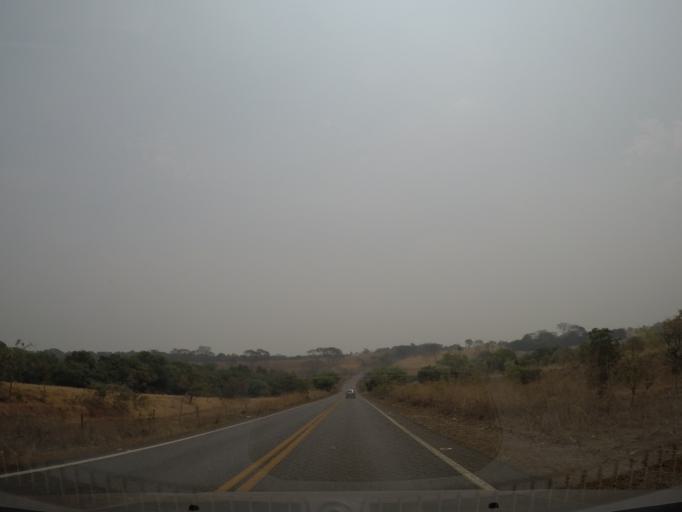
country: BR
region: Goias
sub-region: Pirenopolis
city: Pirenopolis
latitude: -15.8898
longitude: -48.8948
